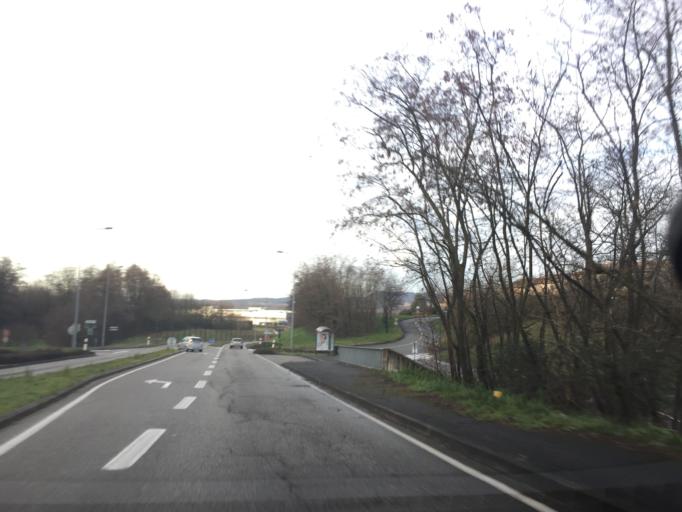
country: FR
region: Rhone-Alpes
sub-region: Departement de l'Isere
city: Vaulx-Milieu
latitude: 45.6147
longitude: 5.1731
